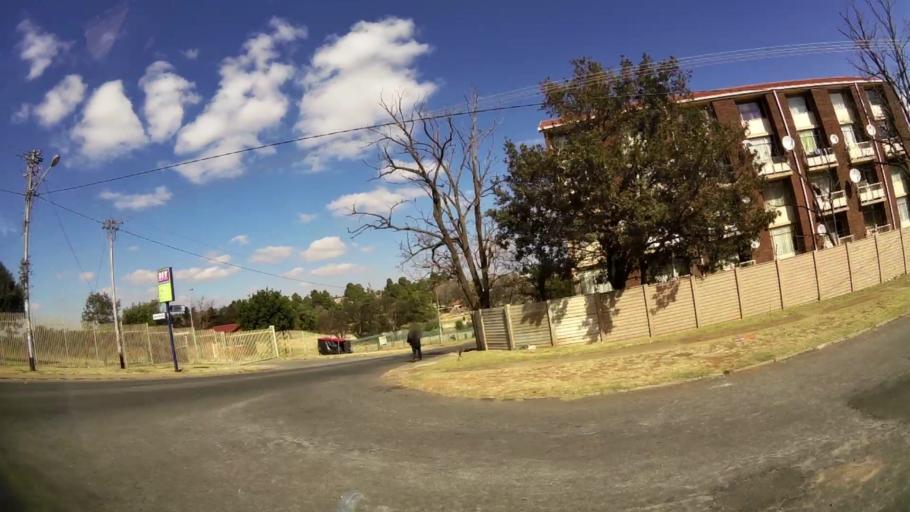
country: ZA
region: Gauteng
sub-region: West Rand District Municipality
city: Krugersdorp
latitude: -26.0993
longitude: 27.7814
